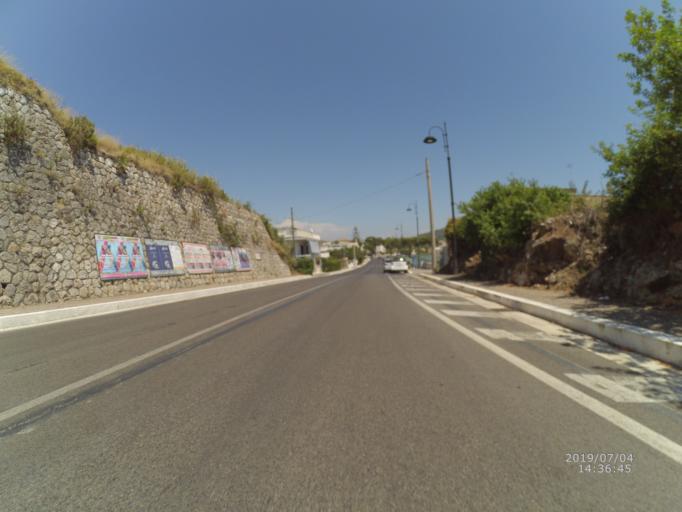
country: IT
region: Latium
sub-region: Provincia di Latina
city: Gaeta
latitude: 41.2118
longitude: 13.5556
